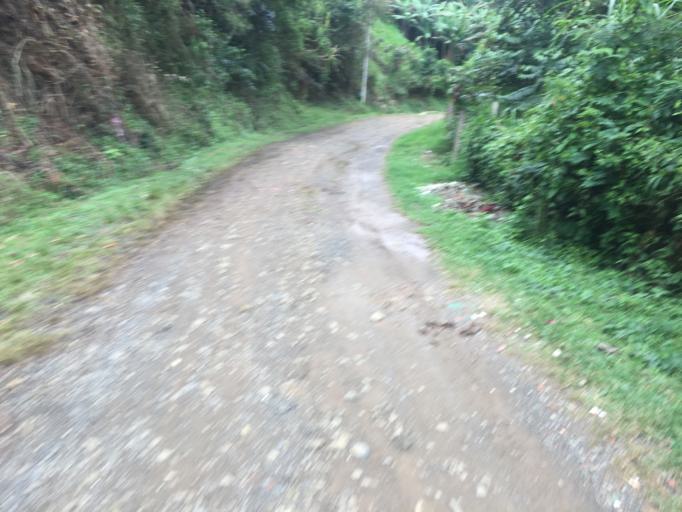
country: CO
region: Valle del Cauca
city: Cali
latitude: 3.4655
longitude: -76.6329
